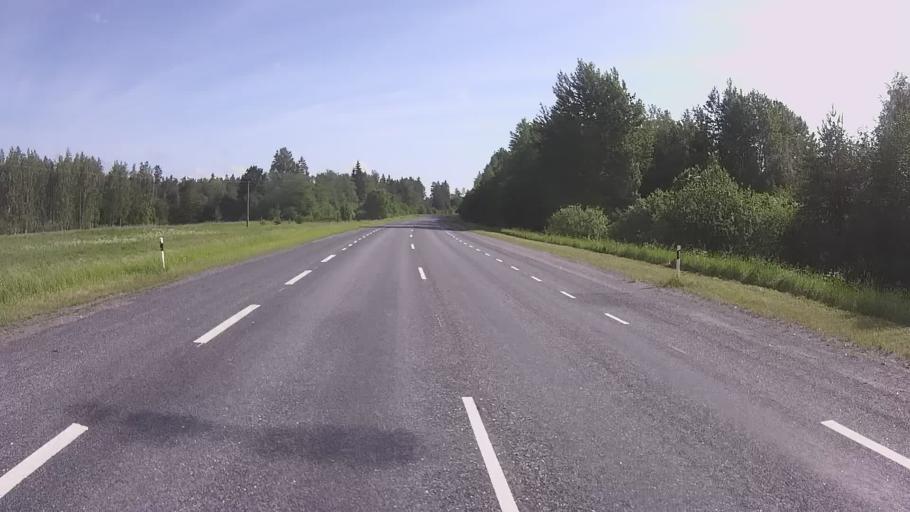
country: EE
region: Valgamaa
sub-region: Torva linn
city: Torva
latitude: 58.0222
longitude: 25.9537
